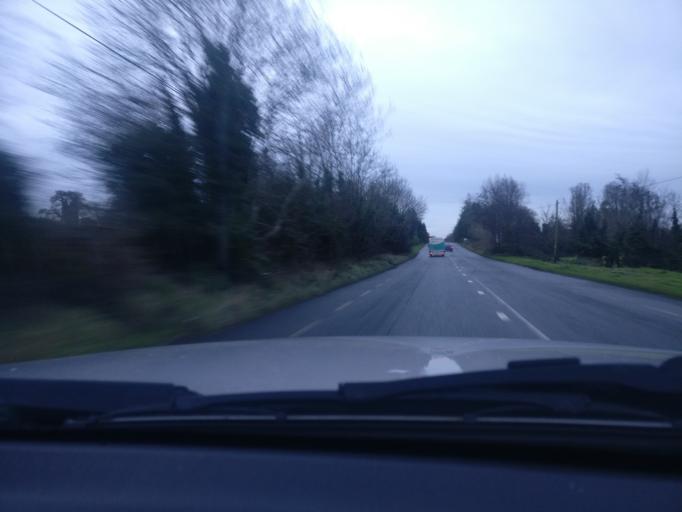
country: IE
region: Leinster
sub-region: An Mhi
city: Kells
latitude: 53.7051
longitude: -6.7967
